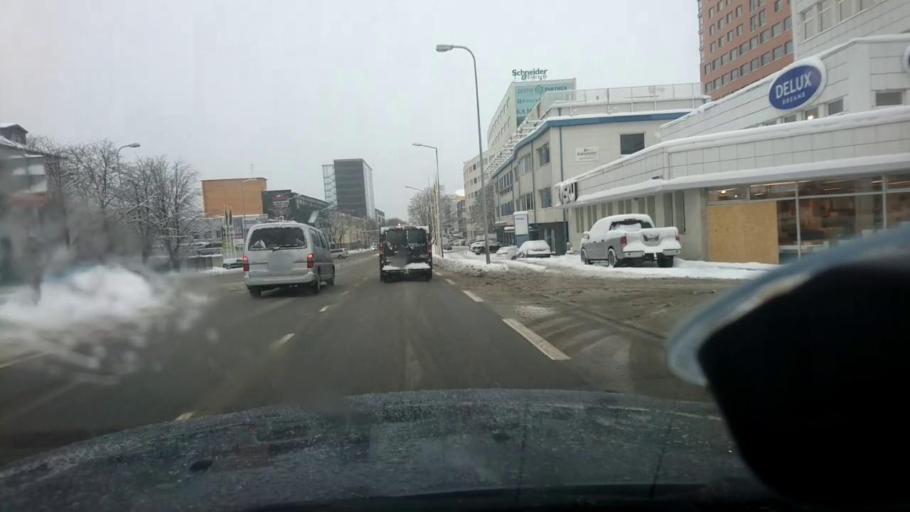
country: EE
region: Harju
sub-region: Tallinna linn
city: Tallinn
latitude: 59.4038
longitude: 24.7306
